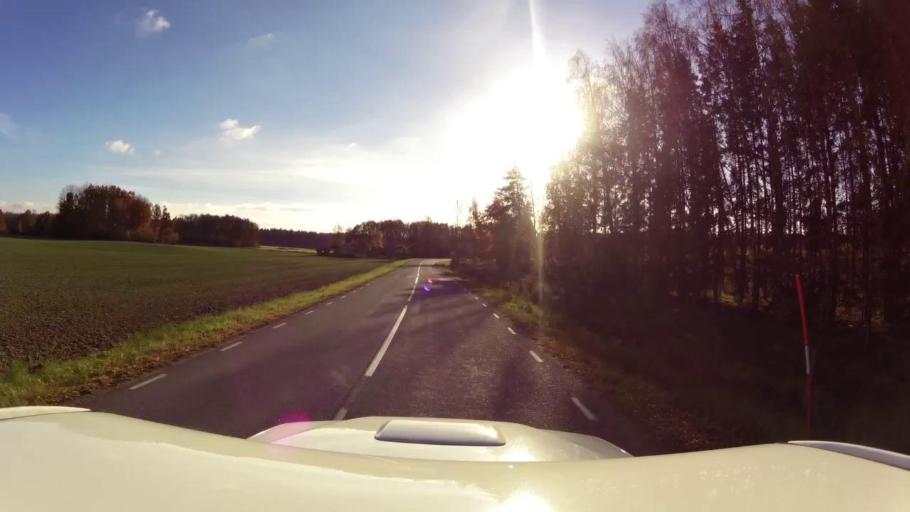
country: SE
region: OEstergoetland
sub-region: Linkopings Kommun
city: Malmslatt
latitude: 58.3219
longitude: 15.5002
